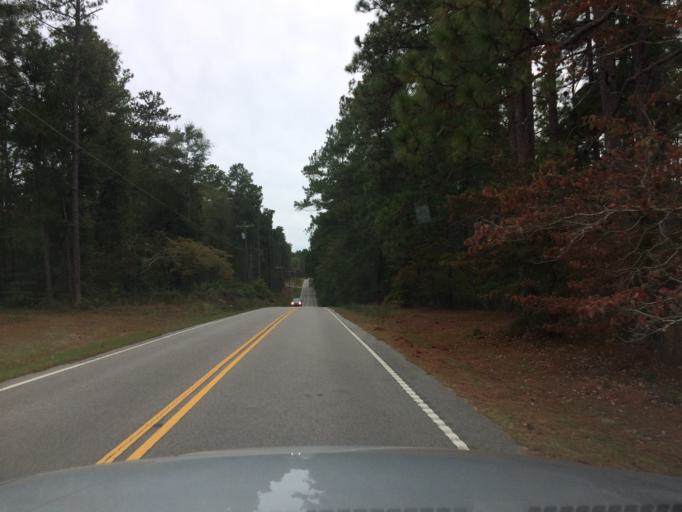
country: US
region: South Carolina
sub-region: Aiken County
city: New Ellenton
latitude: 33.4647
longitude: -81.6659
